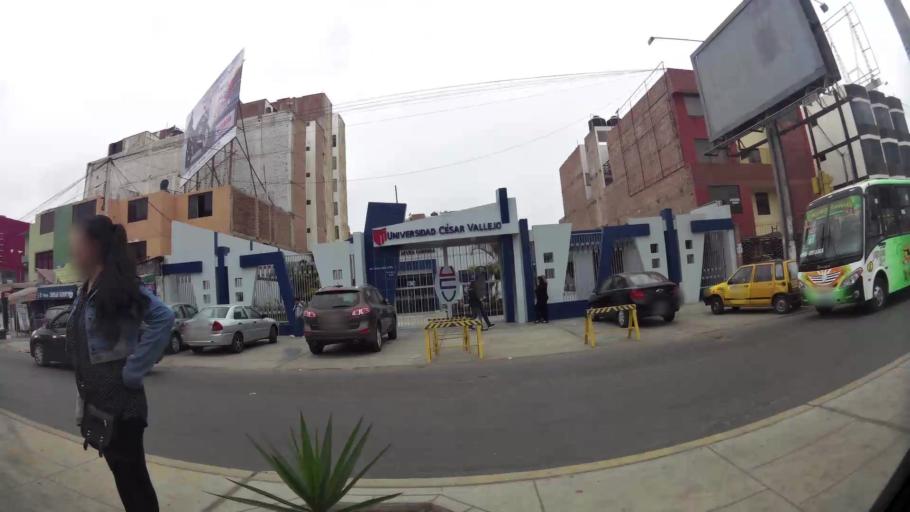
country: PE
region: La Libertad
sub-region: Provincia de Trujillo
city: Buenos Aires
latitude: -8.1294
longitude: -79.0431
